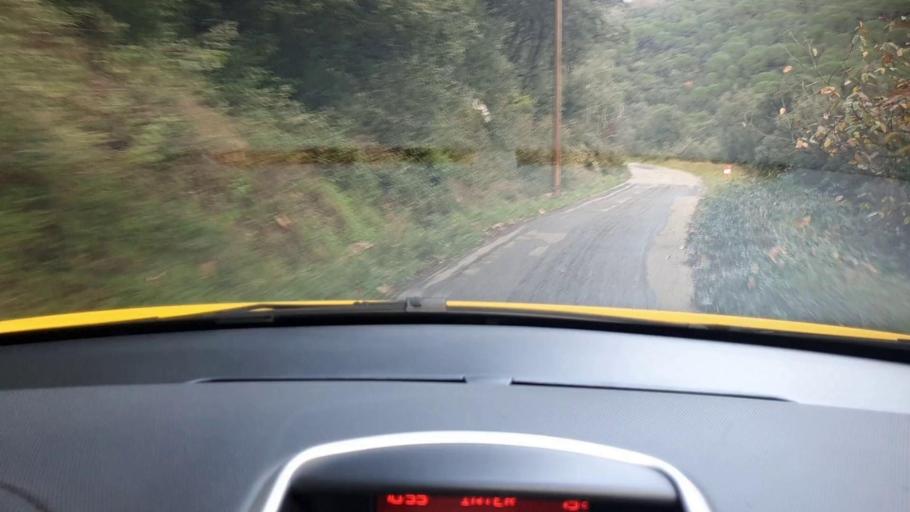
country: FR
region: Languedoc-Roussillon
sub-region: Departement du Gard
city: Lasalle
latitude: 44.0539
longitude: 3.8233
